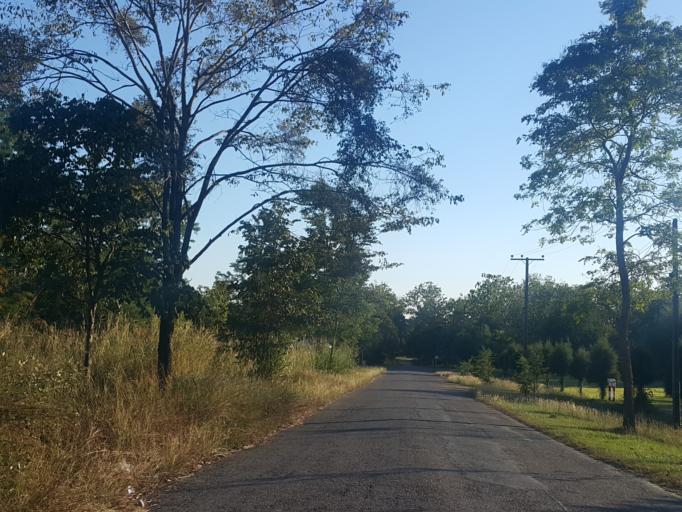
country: TH
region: Chiang Mai
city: San Sai
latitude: 18.9269
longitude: 99.1365
